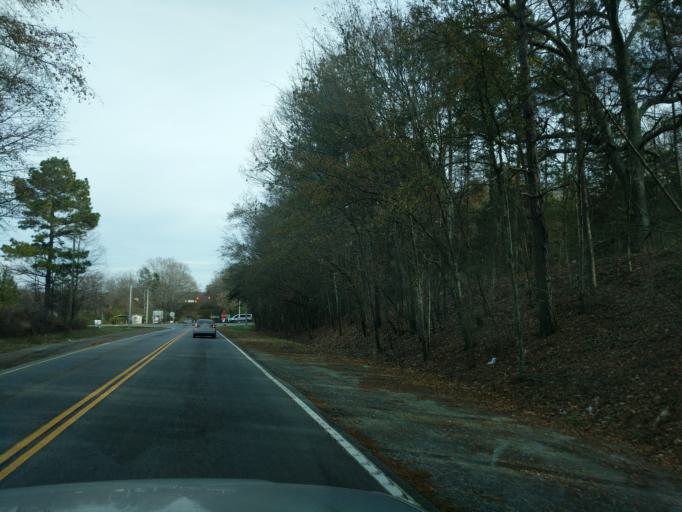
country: US
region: South Carolina
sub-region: Pickens County
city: Liberty
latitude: 34.7057
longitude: -82.6824
